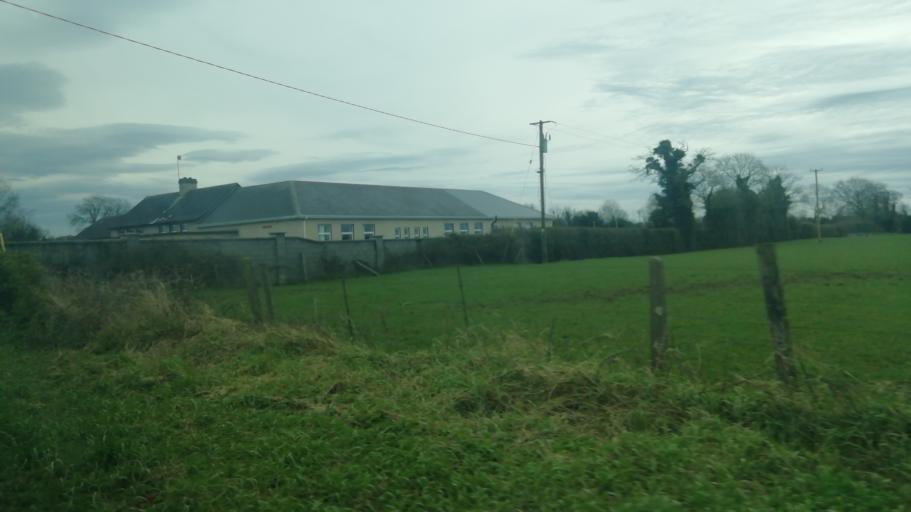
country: IE
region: Leinster
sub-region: Kildare
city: Derrinturn
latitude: 53.3066
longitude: -6.9168
